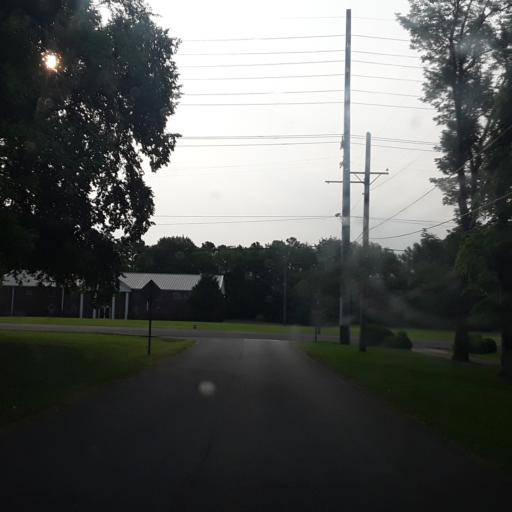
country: US
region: Tennessee
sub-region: Williamson County
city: Brentwood
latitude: 36.0597
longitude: -86.7752
